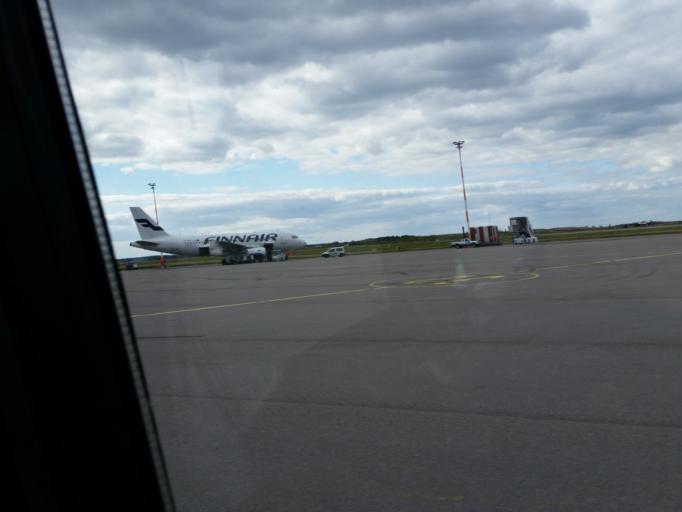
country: FI
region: Uusimaa
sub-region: Helsinki
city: Vantaa
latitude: 60.3178
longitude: 24.9615
